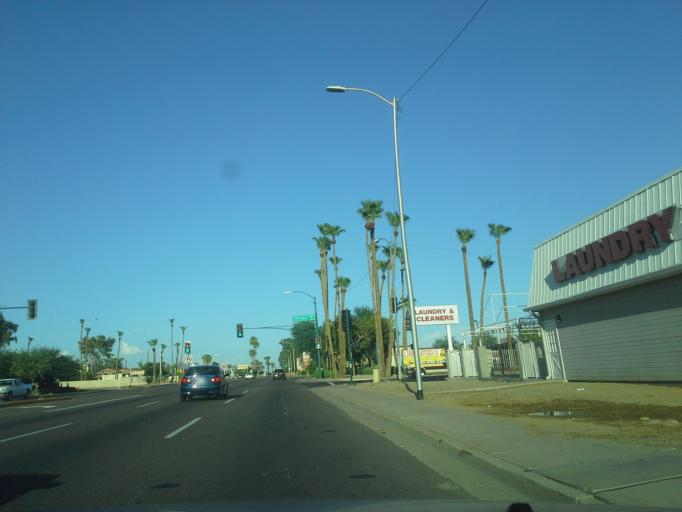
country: US
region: Arizona
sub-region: Maricopa County
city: Glendale
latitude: 33.4948
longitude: -112.1307
